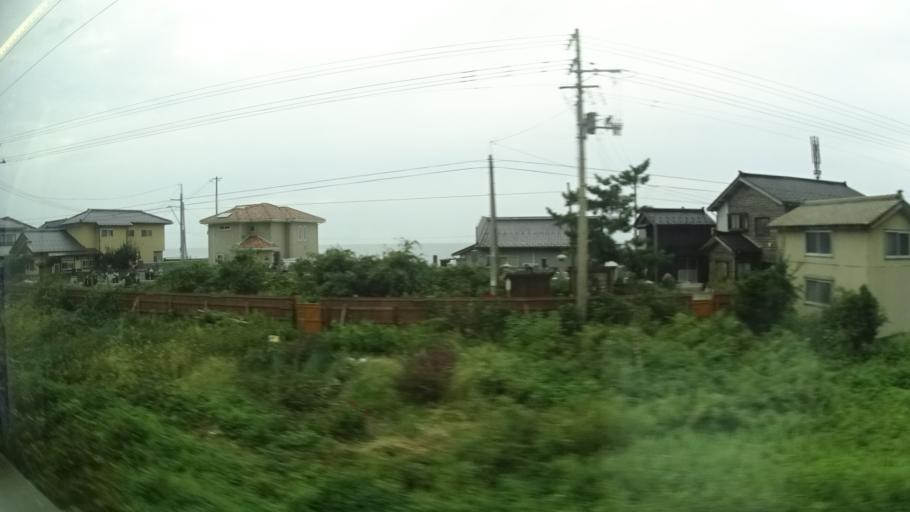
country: JP
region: Yamagata
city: Tsuruoka
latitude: 38.6182
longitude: 139.5831
